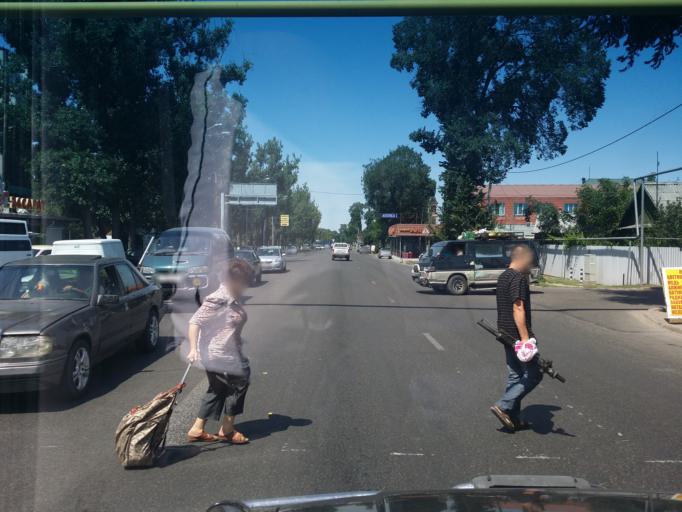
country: KZ
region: Almaty Qalasy
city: Almaty
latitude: 43.2962
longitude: 76.9330
